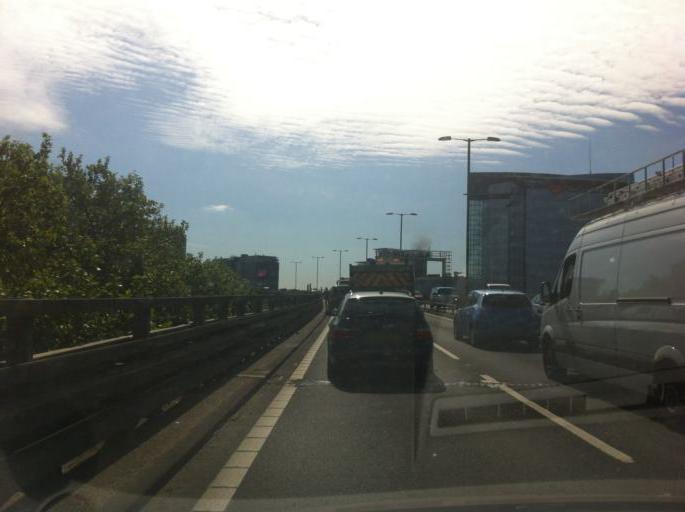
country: GB
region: England
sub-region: Greater London
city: Brentford
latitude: 51.4903
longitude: -0.3191
